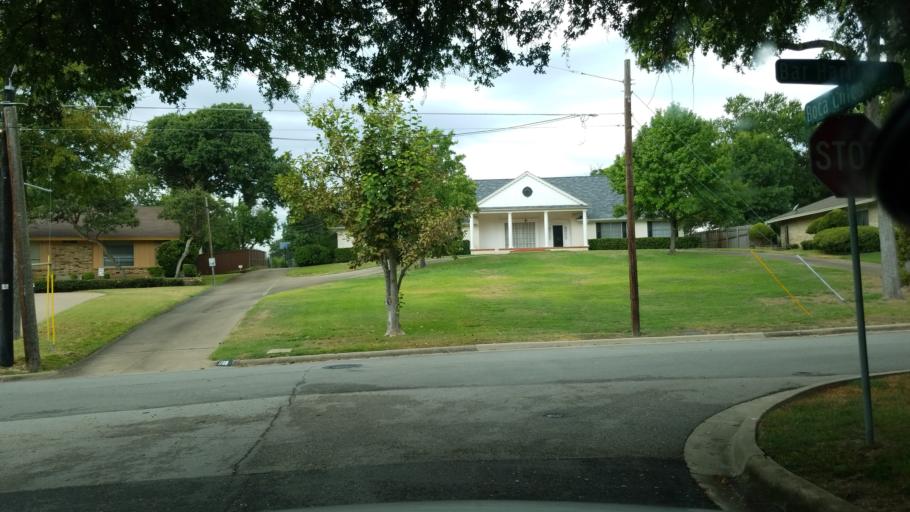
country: US
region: Texas
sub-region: Dallas County
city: Duncanville
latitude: 32.6707
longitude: -96.8491
